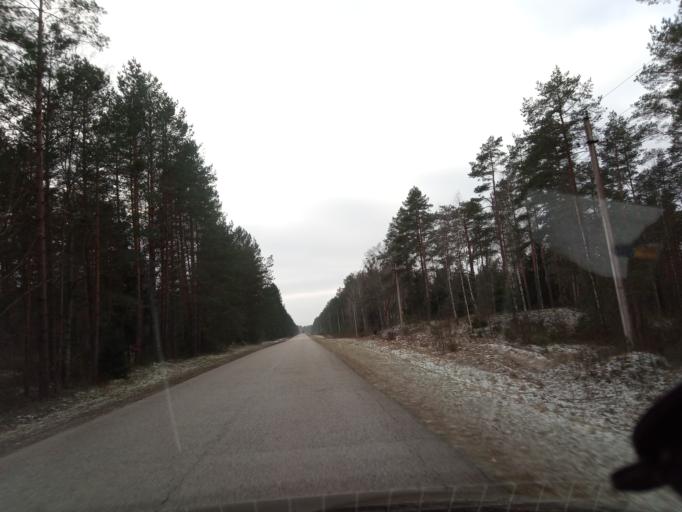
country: LT
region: Alytaus apskritis
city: Varena
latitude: 54.0322
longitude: 24.3621
